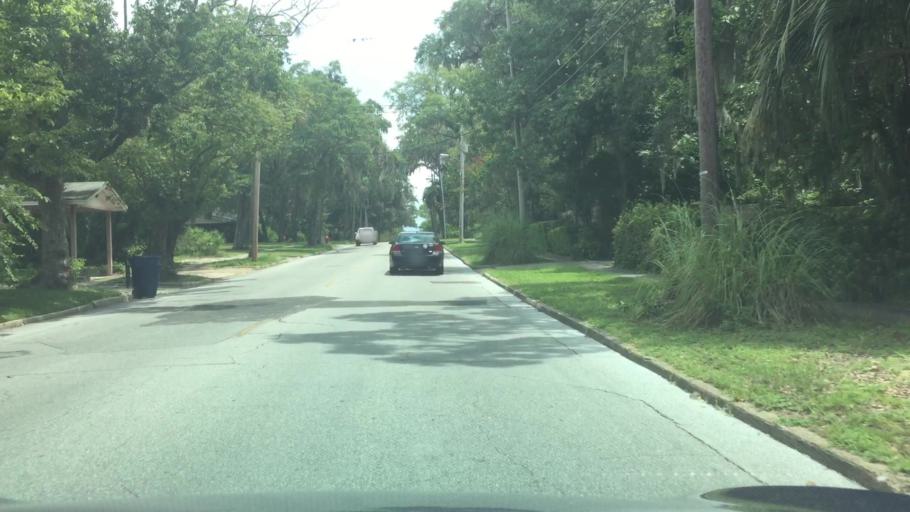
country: US
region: Florida
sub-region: Bay County
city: Panama City
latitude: 30.1459
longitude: -85.6544
